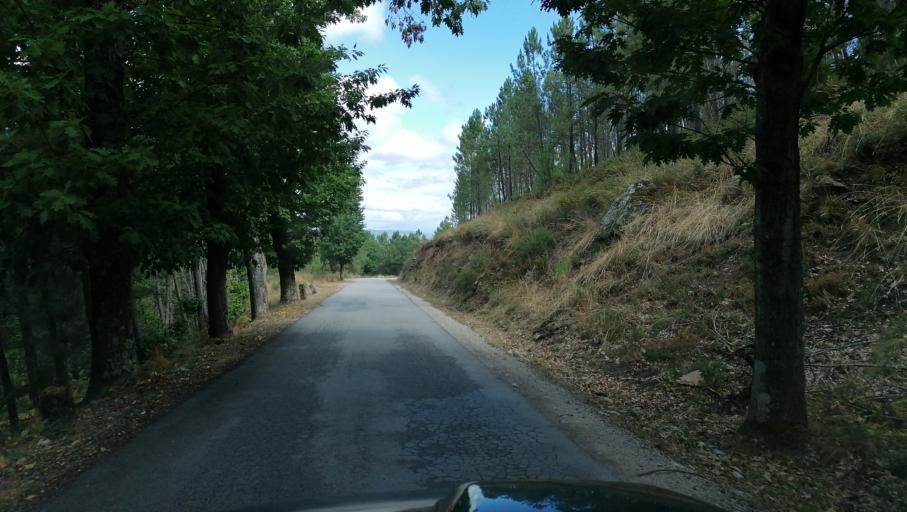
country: PT
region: Vila Real
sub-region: Vila Pouca de Aguiar
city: Vila Pouca de Aguiar
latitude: 41.5318
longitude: -7.5959
